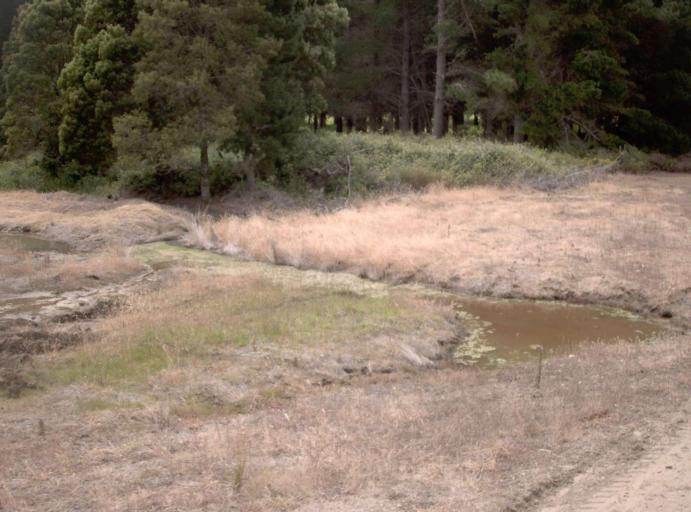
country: AU
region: Victoria
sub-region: Latrobe
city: Traralgon
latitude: -38.3948
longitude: 146.6587
